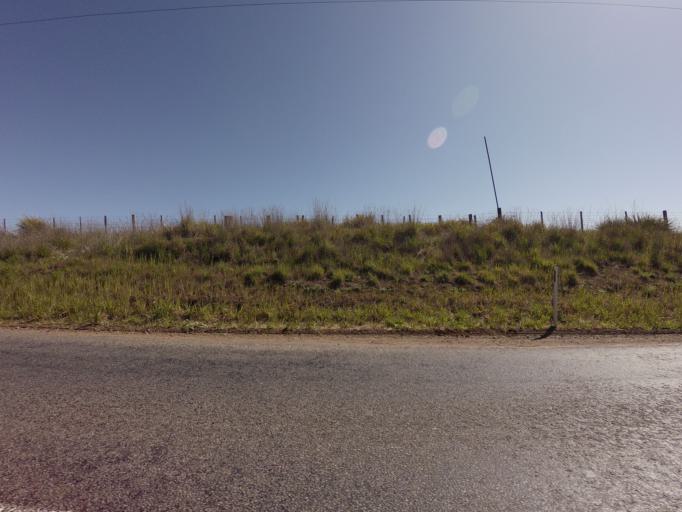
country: AU
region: Tasmania
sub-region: Derwent Valley
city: New Norfolk
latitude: -42.5371
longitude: 146.7533
